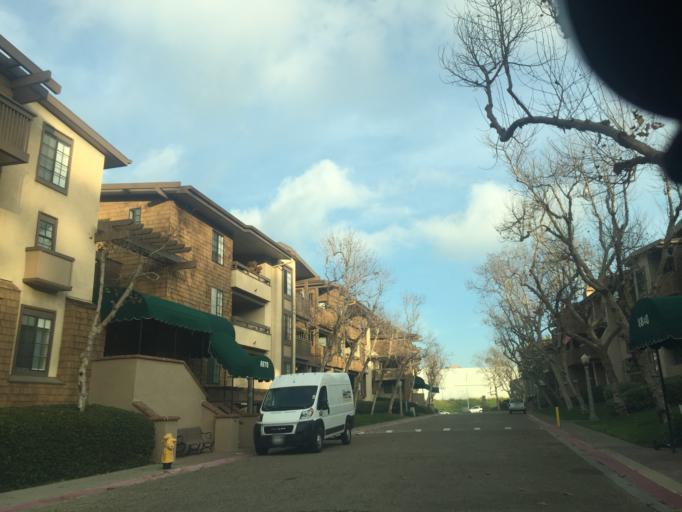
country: US
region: California
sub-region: San Diego County
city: La Jolla
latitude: 32.8696
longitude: -117.2356
